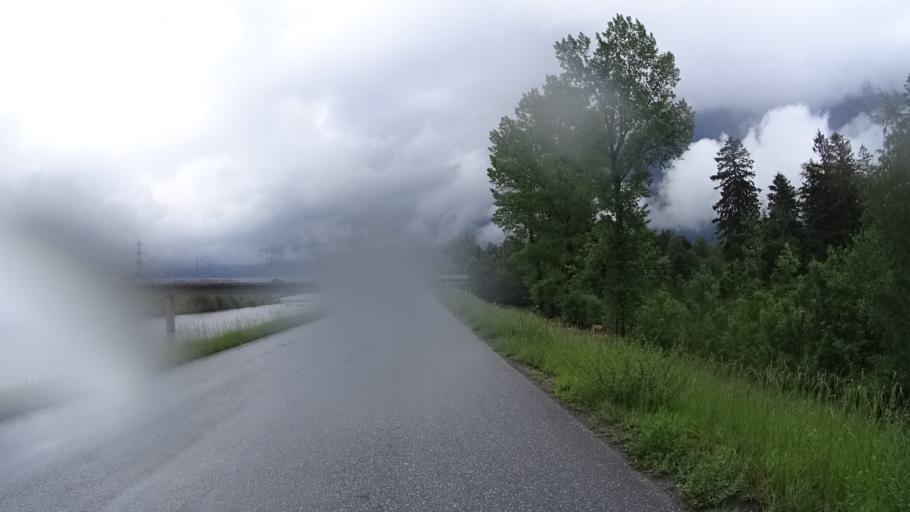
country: LI
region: Balzers
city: Balzers
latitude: 47.0716
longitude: 9.4885
